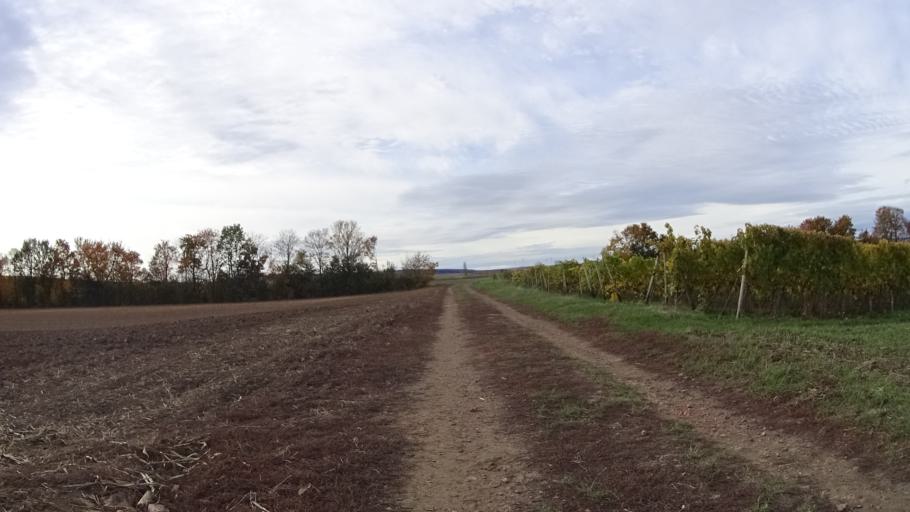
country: DE
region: Rheinland-Pfalz
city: Eckelsheim
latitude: 49.7979
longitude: 7.9935
